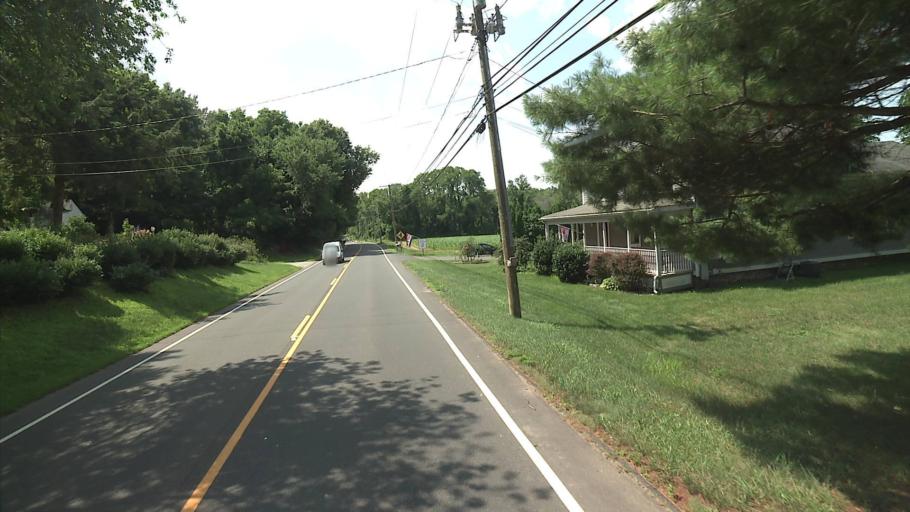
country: US
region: Connecticut
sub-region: Middlesex County
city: Cromwell
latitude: 41.5984
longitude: -72.6047
